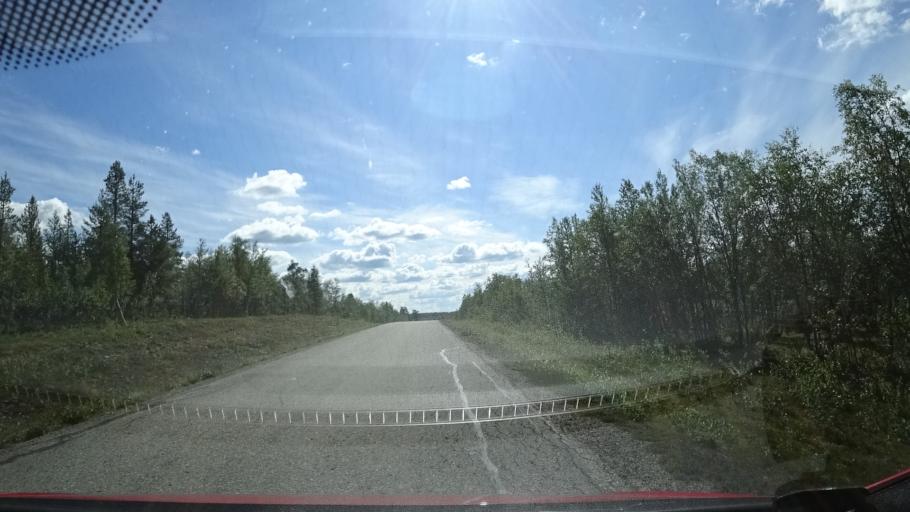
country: FI
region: Lapland
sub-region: Pohjois-Lappi
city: Inari
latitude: 68.5636
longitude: 26.1874
